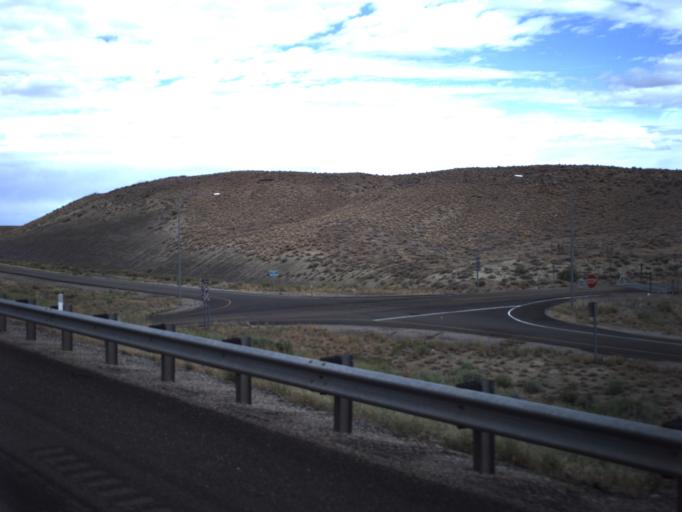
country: US
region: Utah
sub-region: Grand County
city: Moab
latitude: 38.9615
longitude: -109.7231
